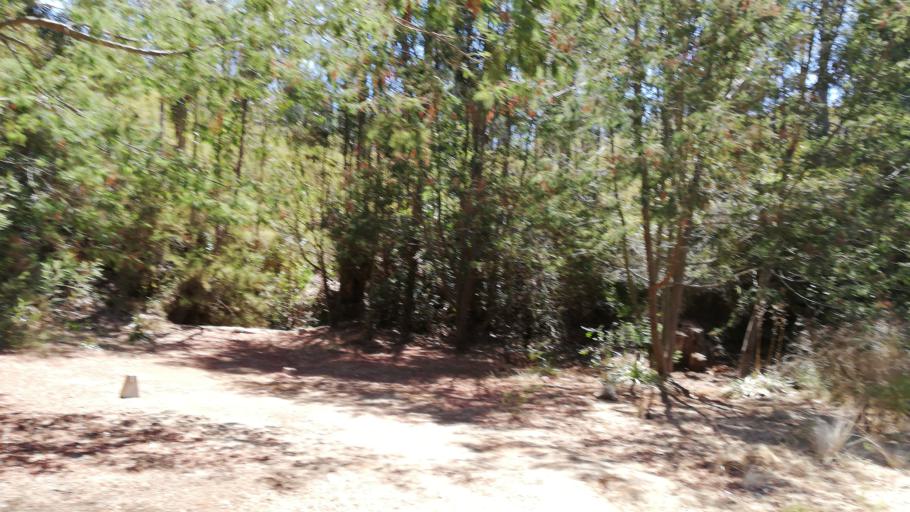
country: CL
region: Valparaiso
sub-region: Provincia de Valparaiso
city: Valparaiso
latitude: -33.0750
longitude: -71.6569
